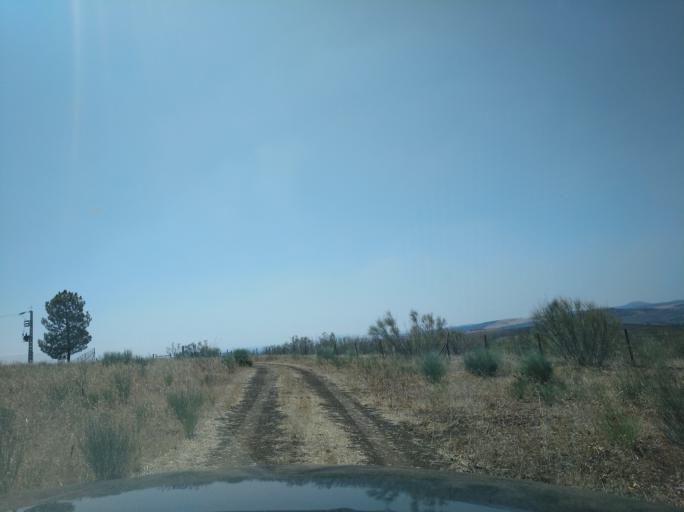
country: PT
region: Portalegre
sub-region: Campo Maior
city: Campo Maior
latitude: 39.0044
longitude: -7.0922
